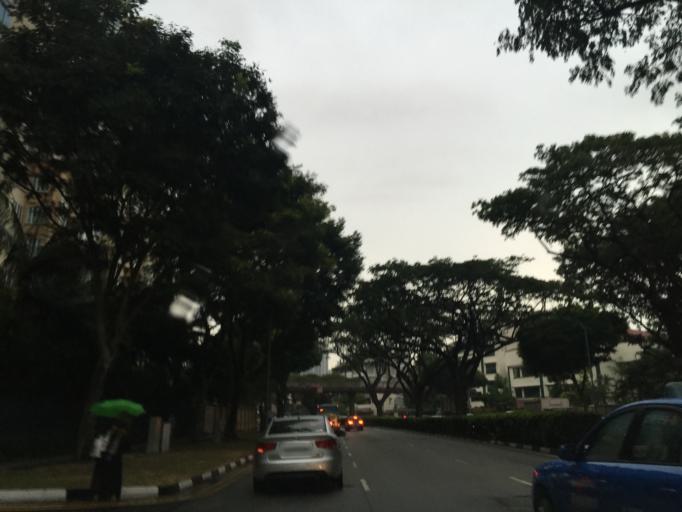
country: SG
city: Singapore
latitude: 1.3187
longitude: 103.8446
